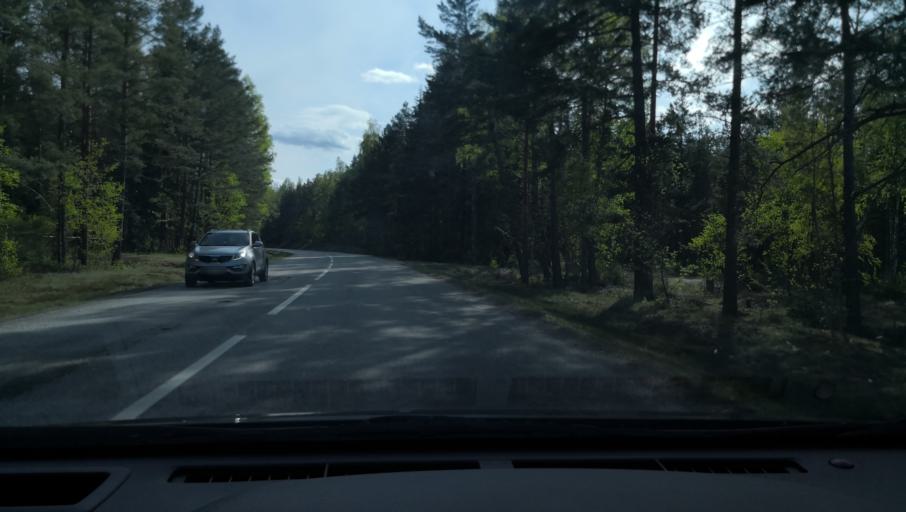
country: SE
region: OErebro
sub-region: Askersunds Kommun
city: Asbro
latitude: 59.0467
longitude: 15.0423
